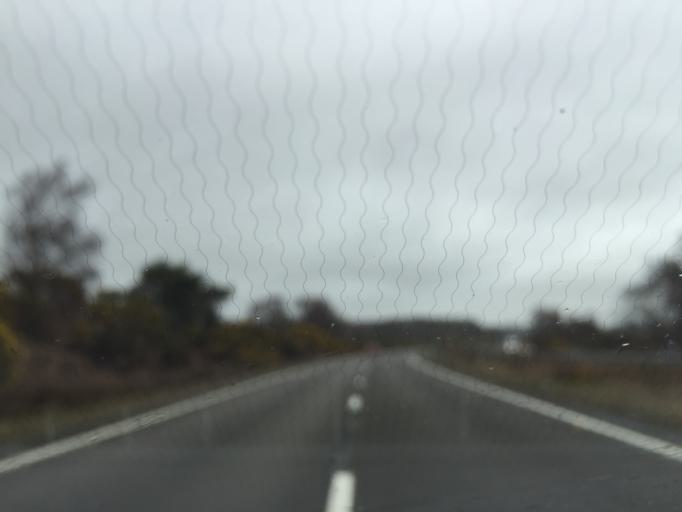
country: GB
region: England
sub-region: Hampshire
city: Cadnam
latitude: 50.8935
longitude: -1.6626
